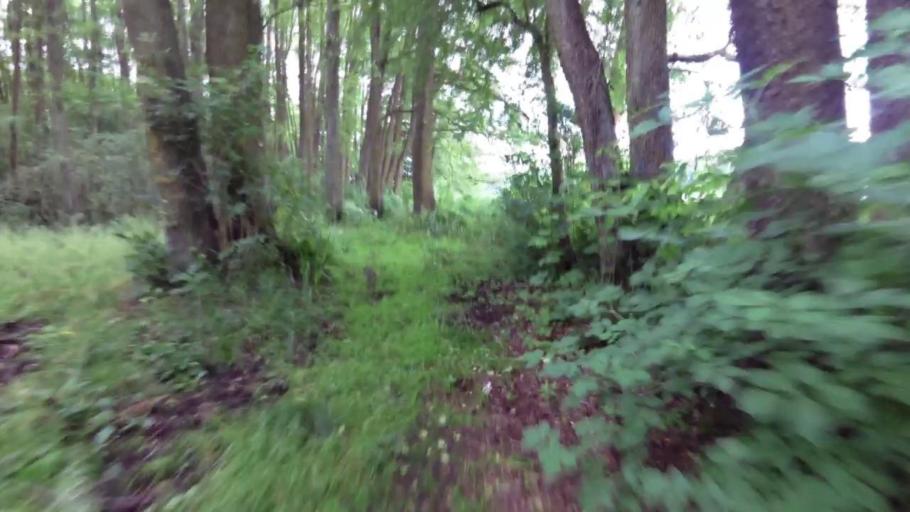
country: PL
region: West Pomeranian Voivodeship
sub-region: Powiat stargardzki
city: Chociwel
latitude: 53.4645
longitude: 15.3531
